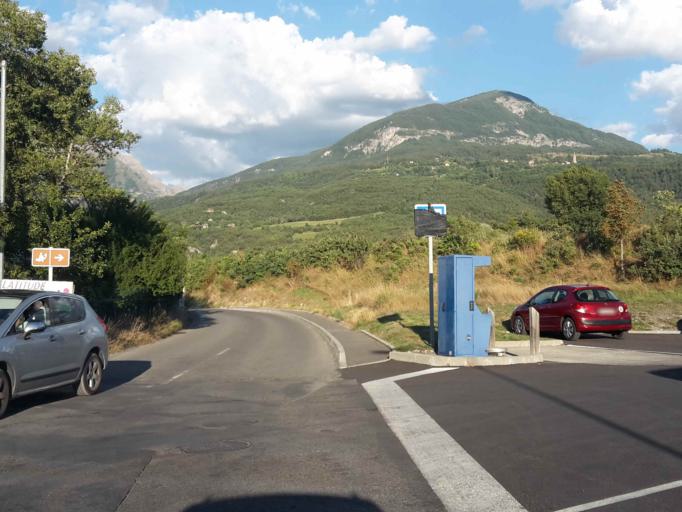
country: FR
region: Provence-Alpes-Cote d'Azur
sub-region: Departement des Hautes-Alpes
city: Embrun
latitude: 44.5509
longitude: 6.4894
